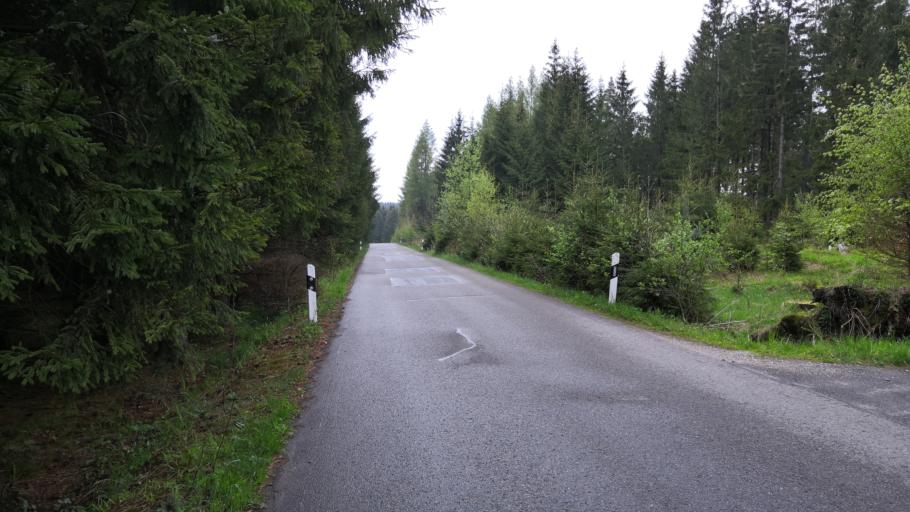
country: DE
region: Saxony
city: Stutzengrun
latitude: 50.5609
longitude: 12.5844
